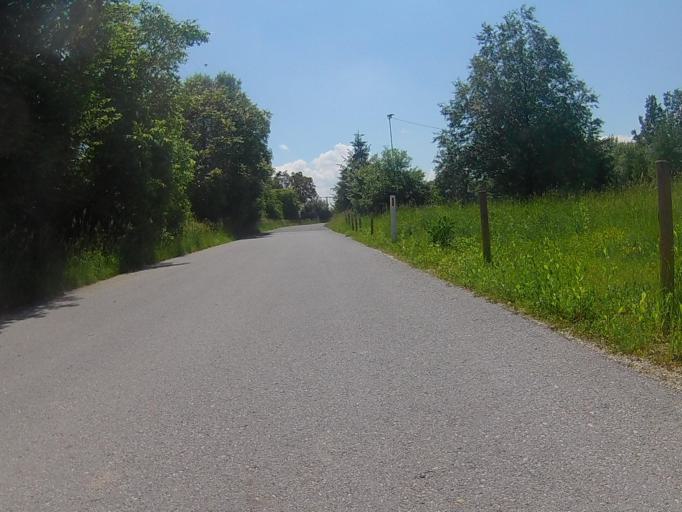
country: SI
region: Hoce-Slivnica
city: Radizel
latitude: 46.4783
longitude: 15.6602
